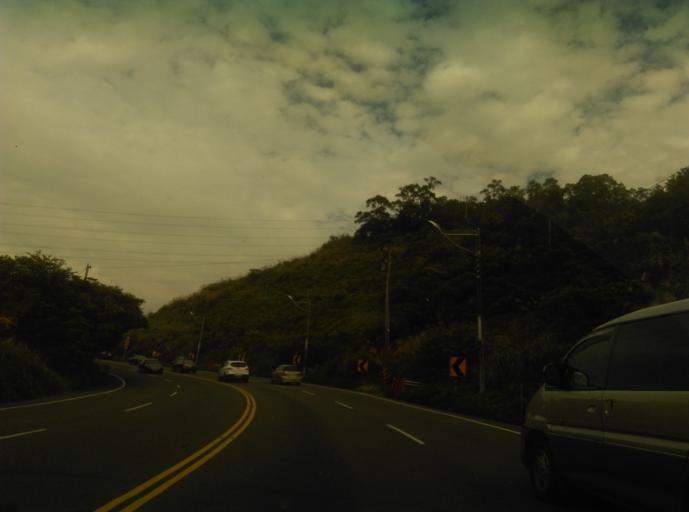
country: TW
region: Taiwan
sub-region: Keelung
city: Keelung
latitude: 25.1571
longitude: 121.6974
